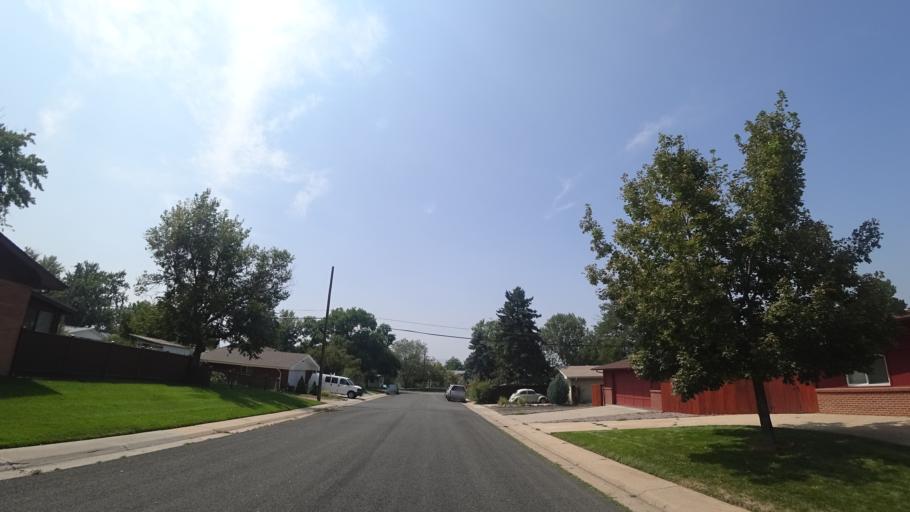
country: US
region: Colorado
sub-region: Arapahoe County
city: Englewood
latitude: 39.6313
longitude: -105.0010
